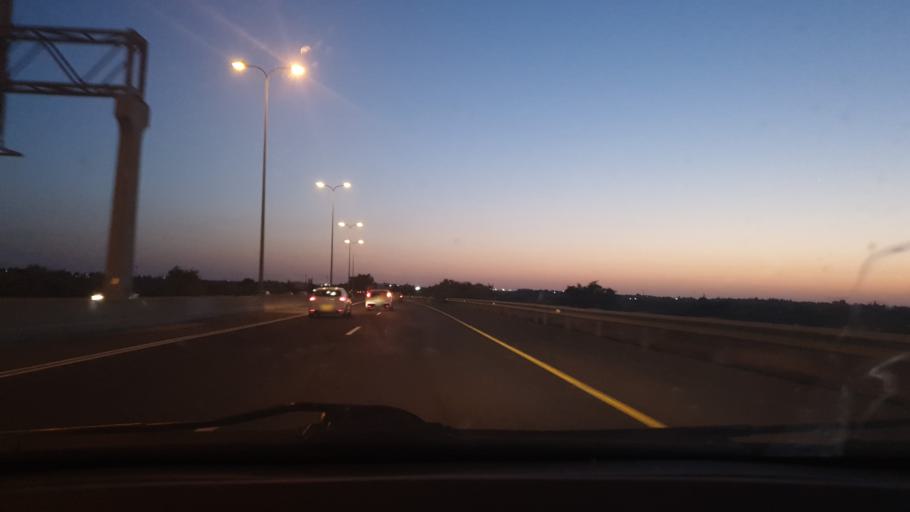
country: IL
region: Central District
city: Gedera
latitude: 31.8054
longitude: 34.8227
